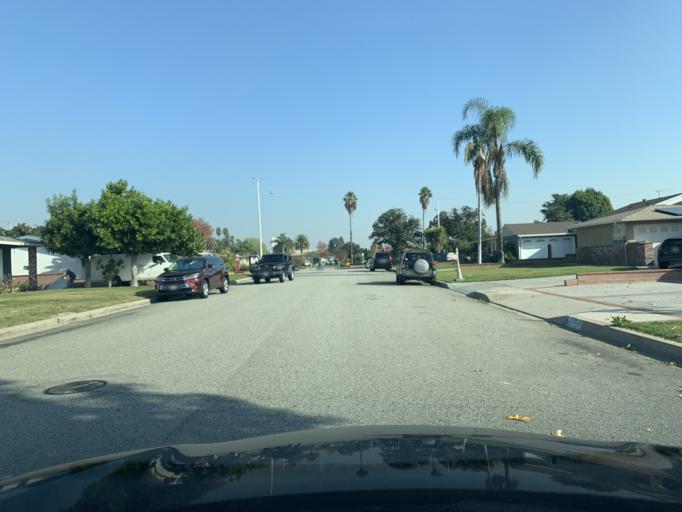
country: US
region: California
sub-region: Los Angeles County
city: Covina
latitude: 34.0746
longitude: -117.8999
